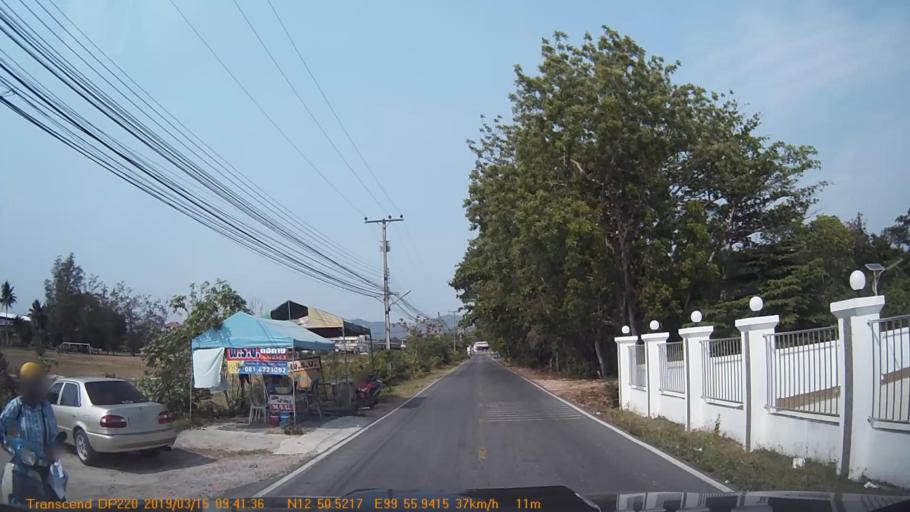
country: TH
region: Phetchaburi
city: Cha-am
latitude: 12.8419
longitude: 99.9322
